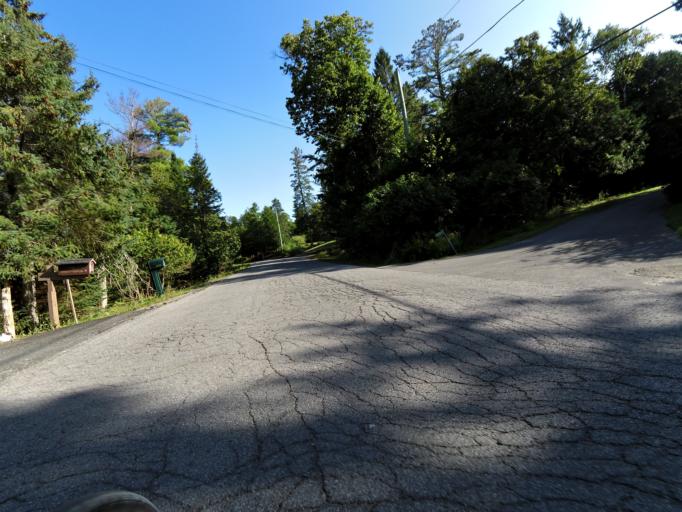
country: CA
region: Ontario
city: Bells Corners
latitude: 45.4853
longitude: -76.0307
